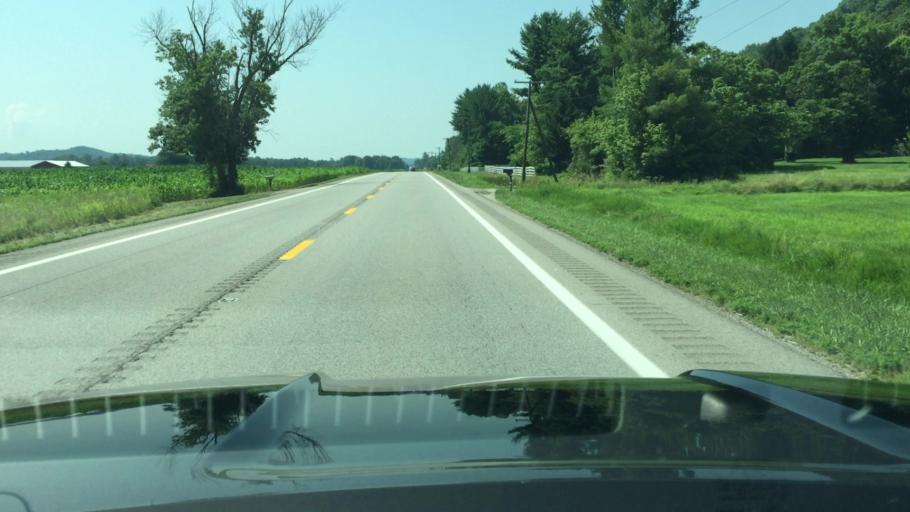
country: US
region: West Virginia
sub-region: Putnam County
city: Buffalo
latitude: 38.7044
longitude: -81.9668
